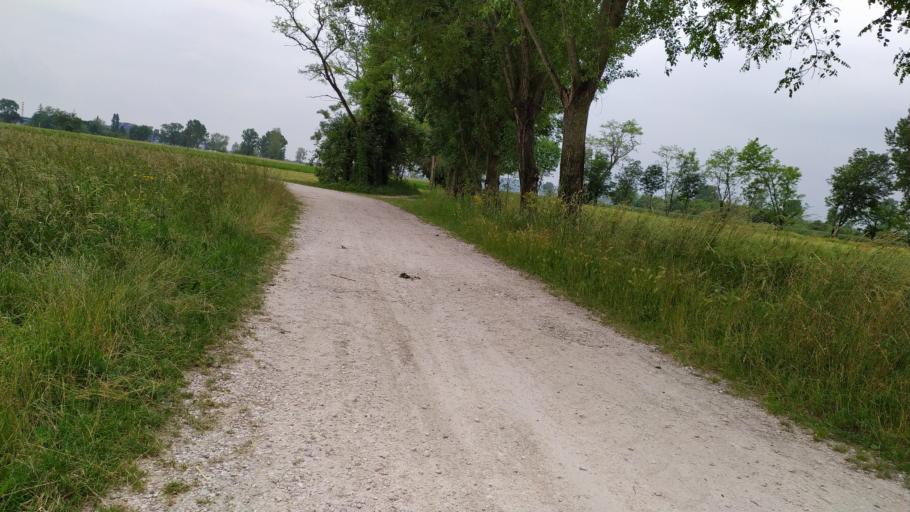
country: IT
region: Friuli Venezia Giulia
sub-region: Provincia di Udine
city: Osoppo
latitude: 46.2419
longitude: 13.0687
